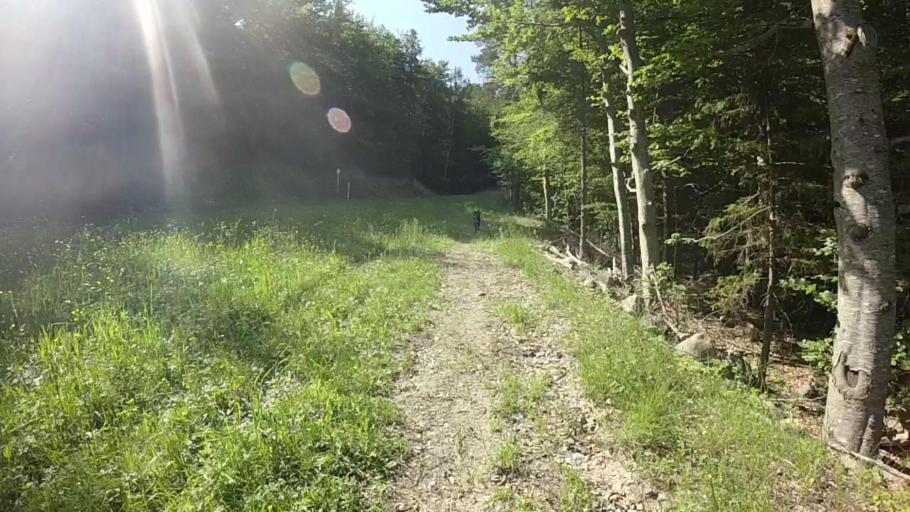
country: FR
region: Provence-Alpes-Cote d'Azur
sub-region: Departement des Alpes-de-Haute-Provence
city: Seyne-les-Alpes
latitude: 44.4082
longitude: 6.3521
